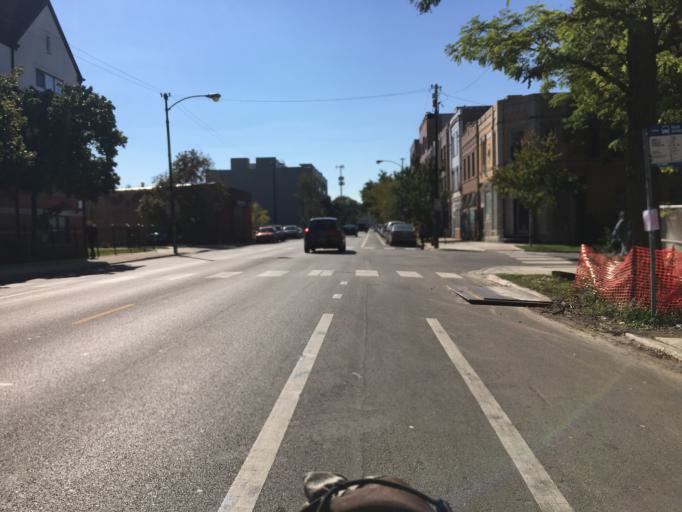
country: US
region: Illinois
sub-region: Cook County
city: Chicago
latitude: 41.8983
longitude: -87.6969
